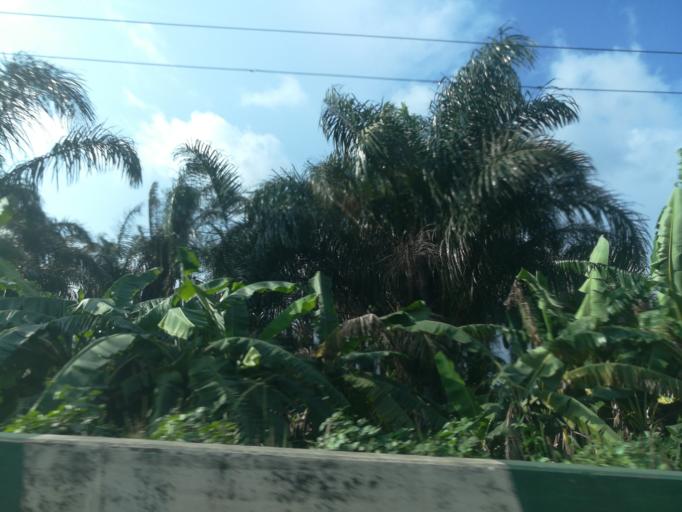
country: NG
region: Ogun
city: Ado Odo
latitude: 6.4867
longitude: 3.0657
